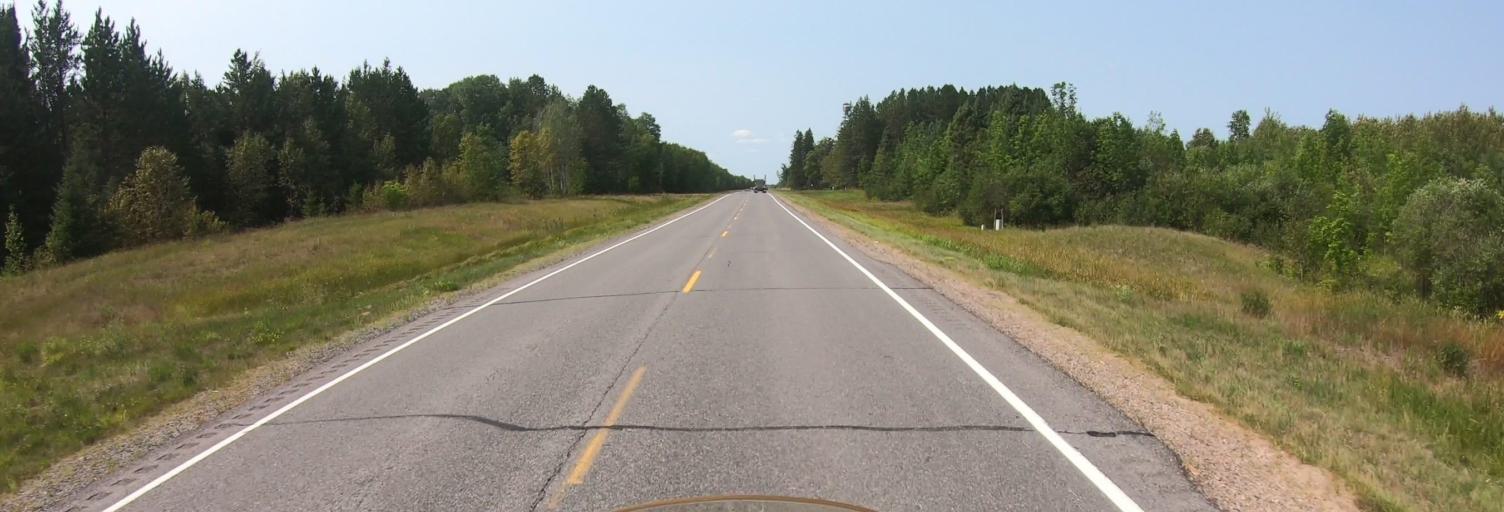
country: US
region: Minnesota
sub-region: Koochiching County
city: International Falls
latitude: 48.5127
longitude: -93.7770
